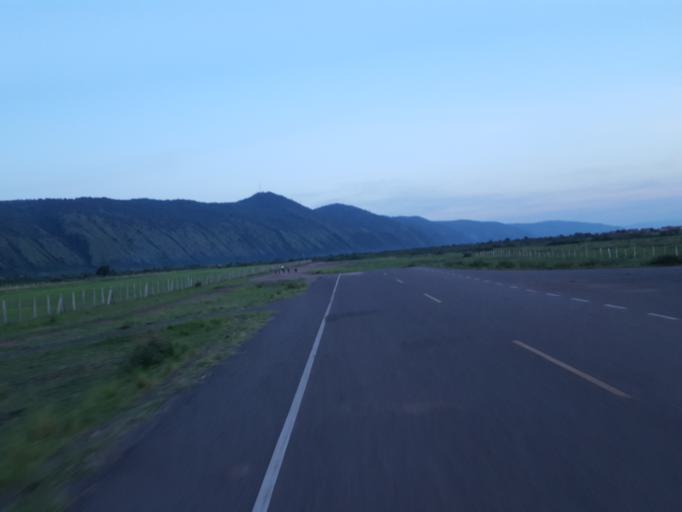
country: UG
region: Western Region
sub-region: Kibale District
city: Kagadi
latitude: 1.2446
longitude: 30.7472
